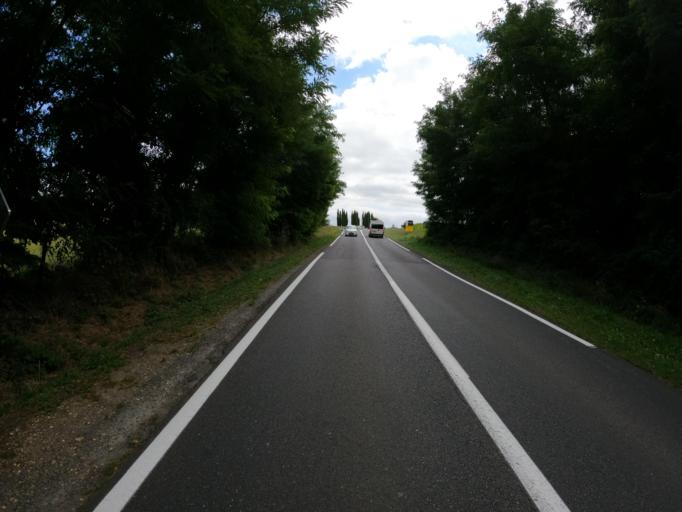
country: FR
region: Poitou-Charentes
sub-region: Departement de la Vienne
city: Charroux
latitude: 46.1538
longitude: 0.3714
